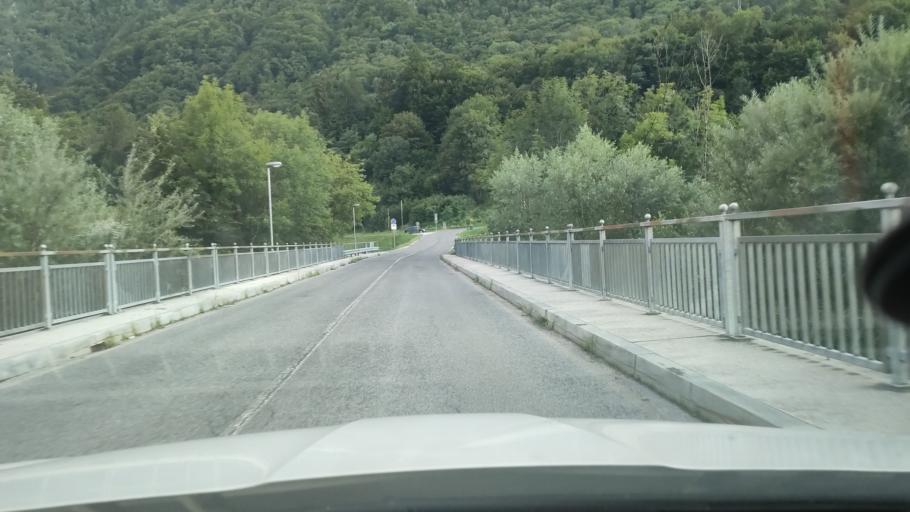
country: IT
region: Friuli Venezia Giulia
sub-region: Provincia di Udine
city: Cras
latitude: 46.2106
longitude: 13.6354
